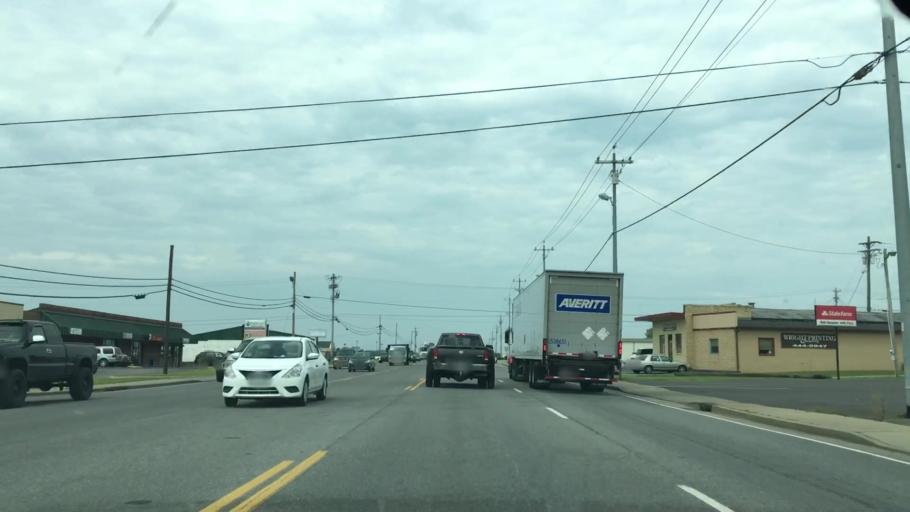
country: US
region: Tennessee
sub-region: Wilson County
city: Lebanon
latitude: 36.2148
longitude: -86.3260
